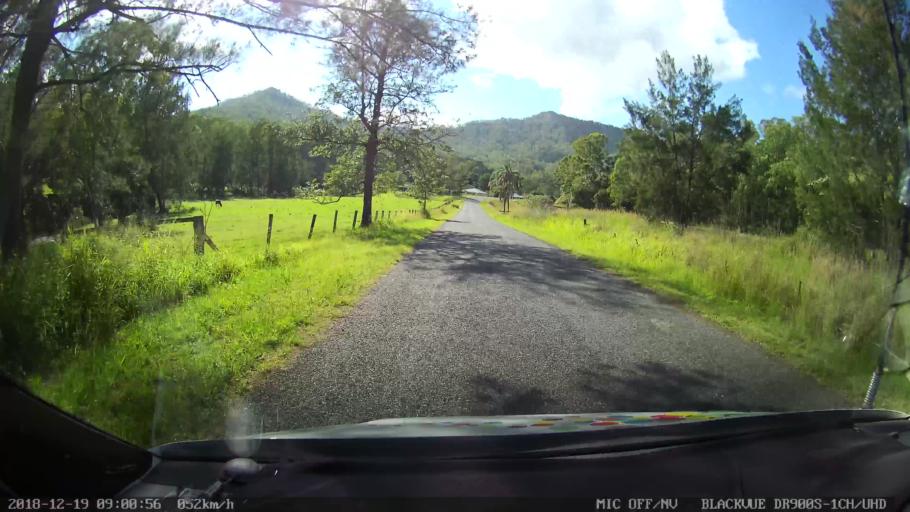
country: AU
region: New South Wales
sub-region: Kyogle
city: Kyogle
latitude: -28.4355
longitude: 152.9576
